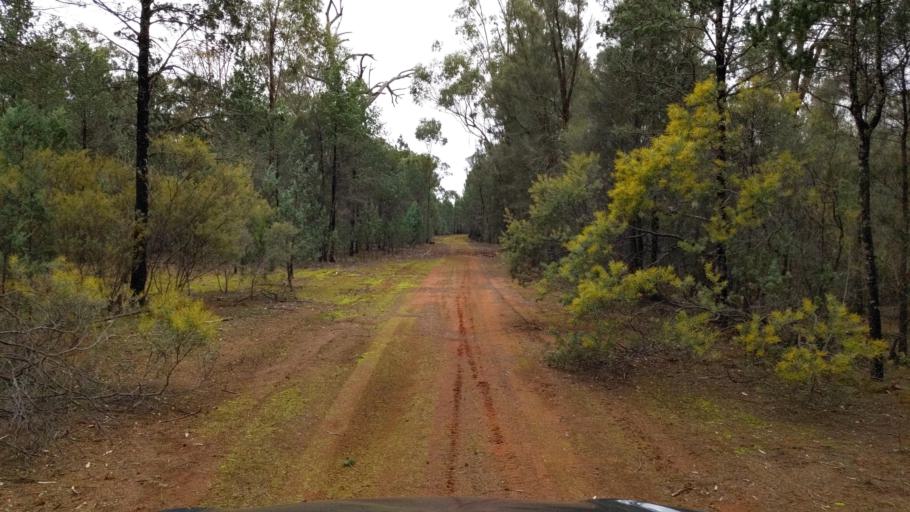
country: AU
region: New South Wales
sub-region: Coolamon
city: Coolamon
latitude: -34.8320
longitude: 146.9352
